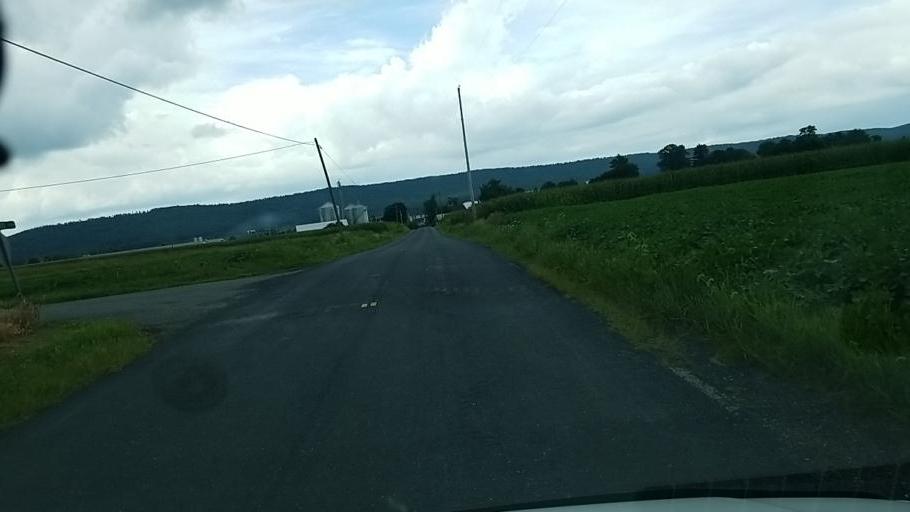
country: US
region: Pennsylvania
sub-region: Dauphin County
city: Elizabethville
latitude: 40.5813
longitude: -76.8499
